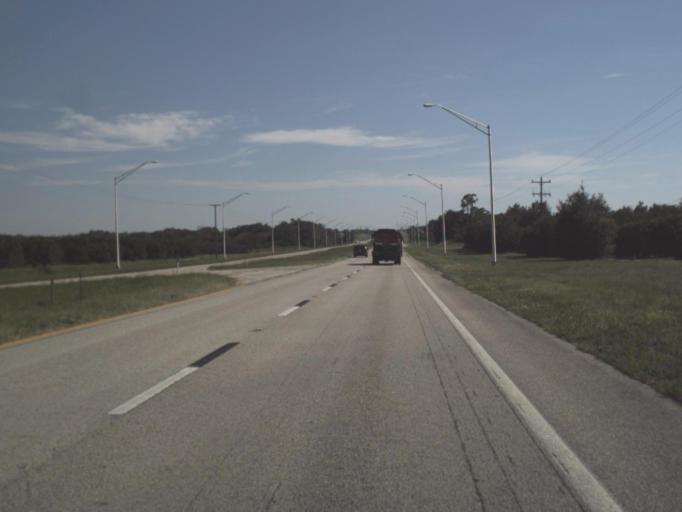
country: US
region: Florida
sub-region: Highlands County
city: Lake Placid
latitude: 27.3789
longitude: -81.4057
